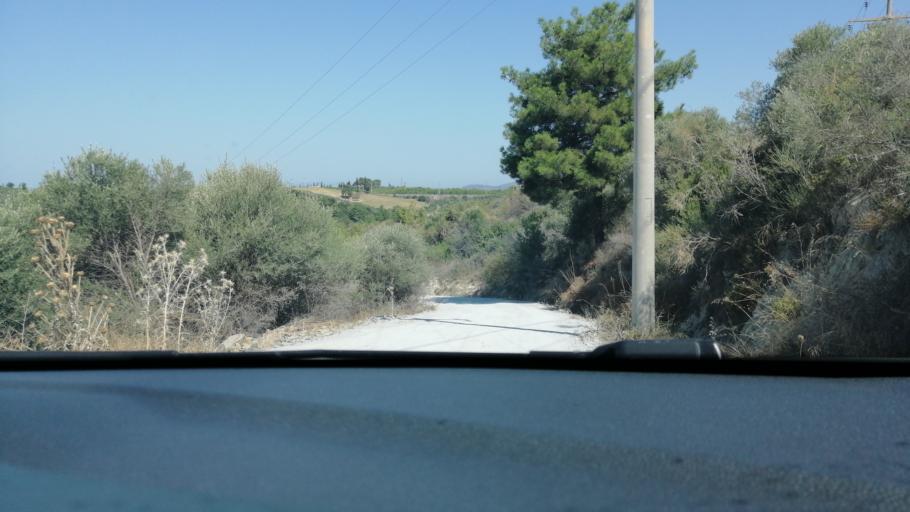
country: TR
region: Aydin
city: Davutlar
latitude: 37.7796
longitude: 27.3144
